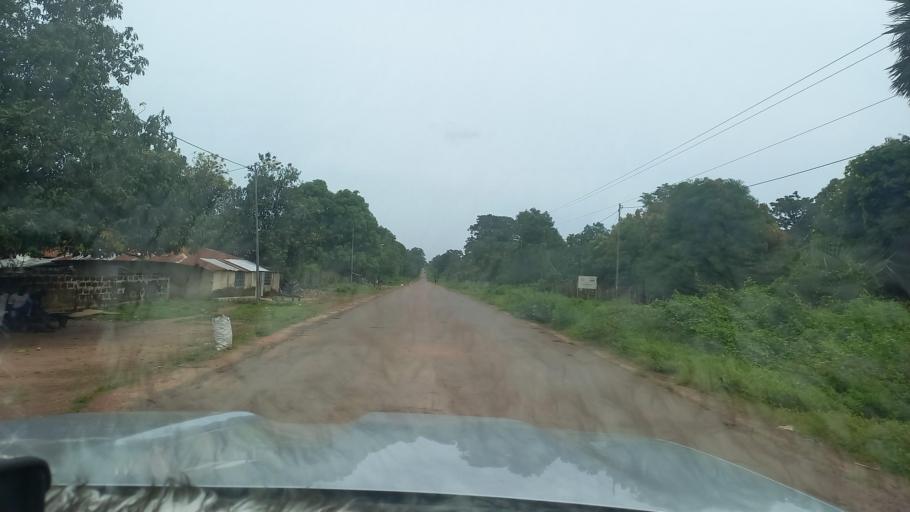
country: SN
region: Ziguinchor
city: Bignona
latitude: 12.8207
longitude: -16.1791
